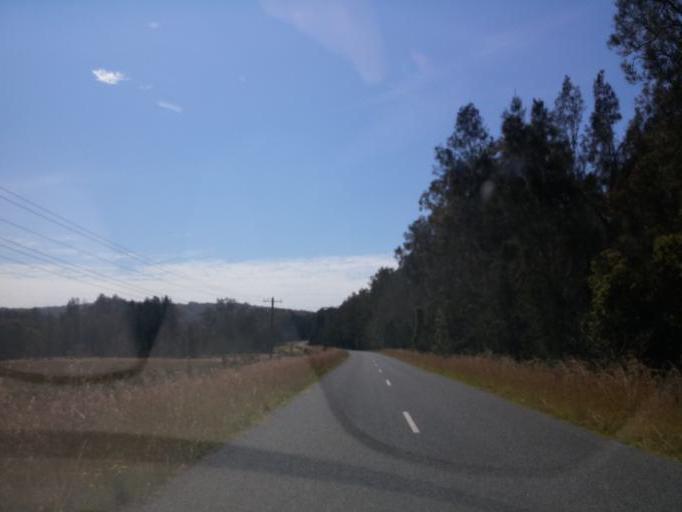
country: AU
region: New South Wales
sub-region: Great Lakes
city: Bulahdelah
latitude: -32.3850
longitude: 152.3401
